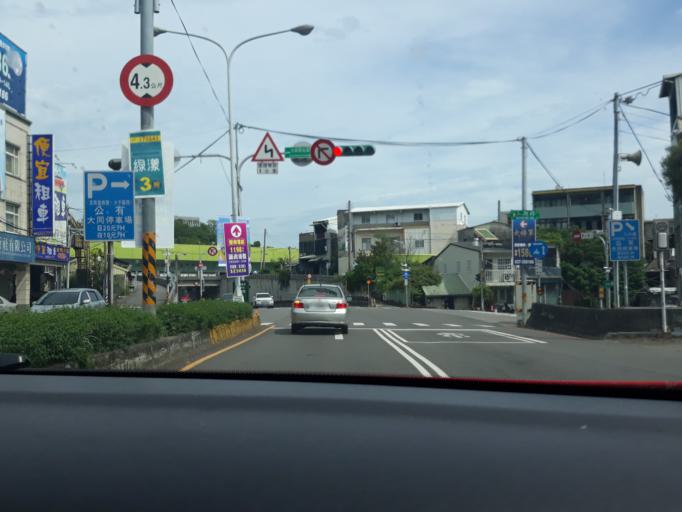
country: TW
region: Taiwan
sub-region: Miaoli
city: Miaoli
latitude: 24.5546
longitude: 120.8142
